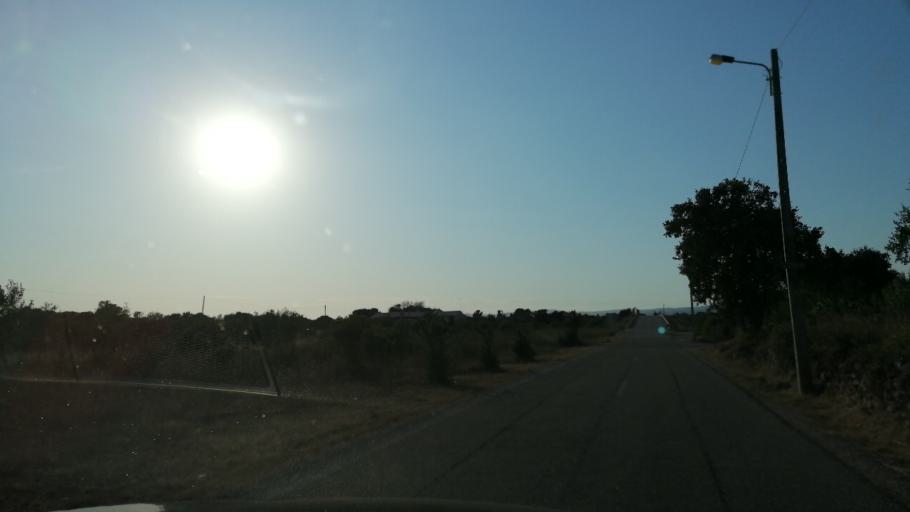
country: PT
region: Santarem
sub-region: Alcanena
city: Alcanena
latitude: 39.4533
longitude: -8.6265
